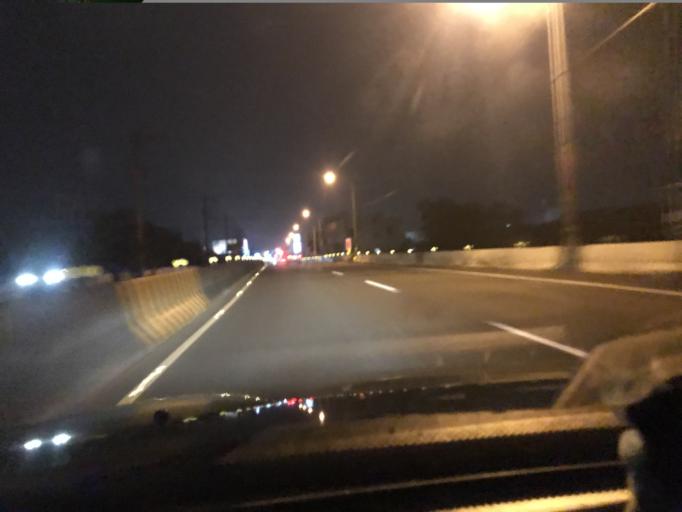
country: TW
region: Taiwan
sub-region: Hsinchu
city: Zhubei
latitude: 24.7776
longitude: 121.0714
